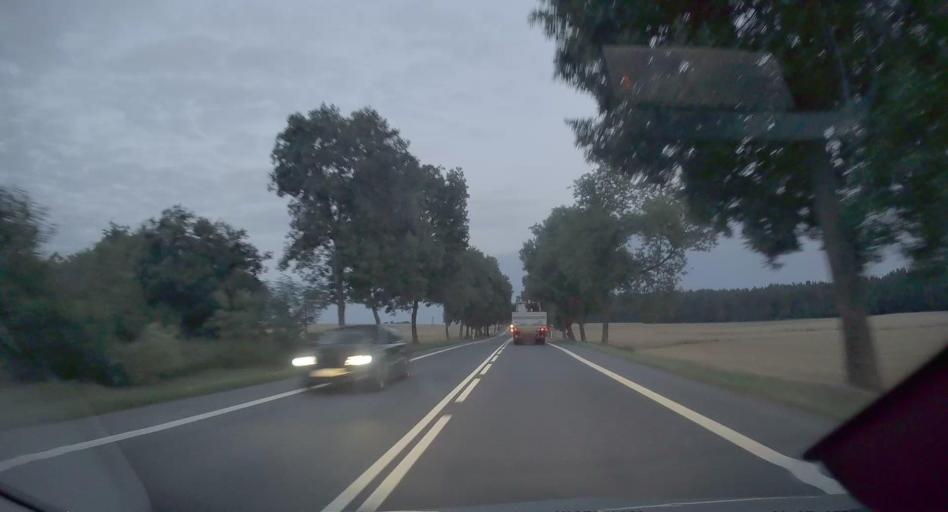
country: PL
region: Silesian Voivodeship
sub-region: Powiat klobucki
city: Opatow
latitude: 50.9474
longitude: 18.8296
